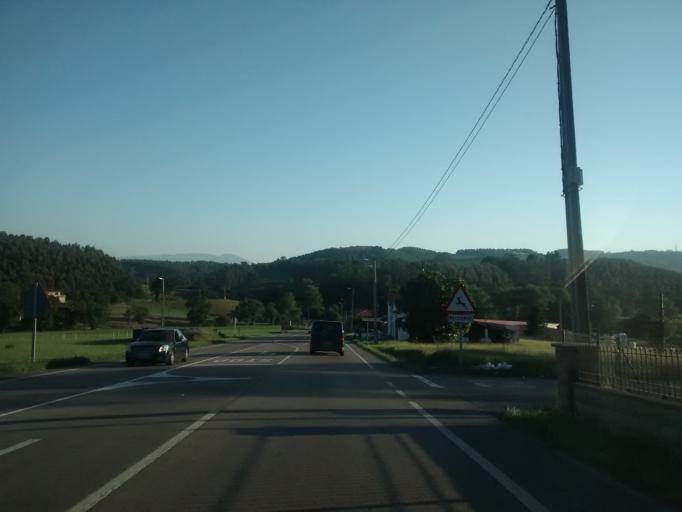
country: ES
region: Cantabria
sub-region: Provincia de Cantabria
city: San Miguel de Meruelo
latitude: 43.4420
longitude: -3.5671
